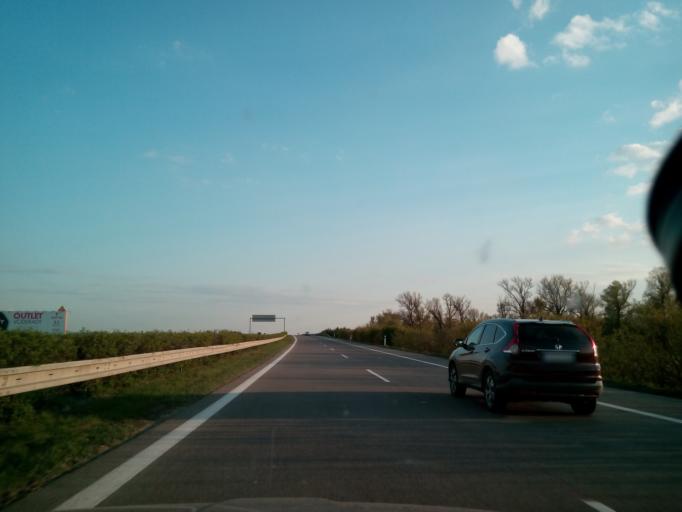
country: SK
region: Trenciansky
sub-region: Okres Nove Mesto nad Vahom
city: Nove Mesto nad Vahom
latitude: 48.7518
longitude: 17.8611
